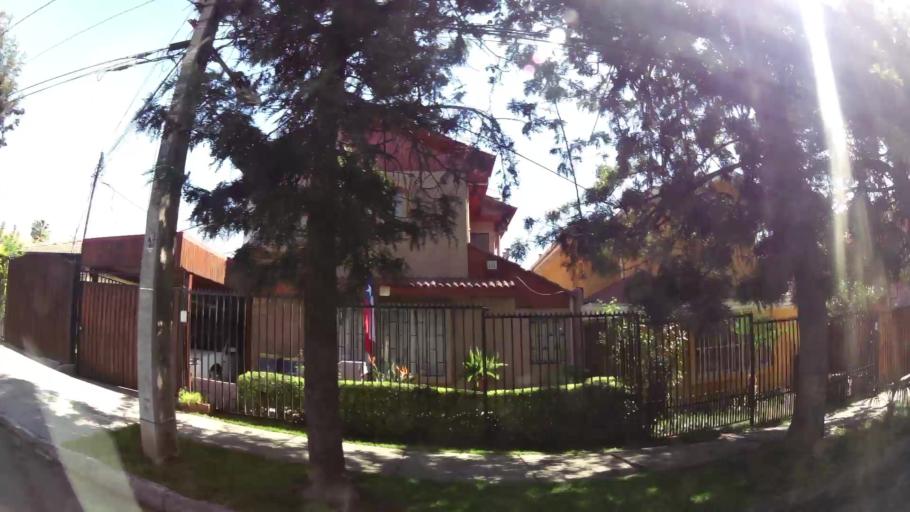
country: CL
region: Santiago Metropolitan
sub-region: Provincia de Santiago
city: Villa Presidente Frei, Nunoa, Santiago, Chile
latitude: -33.5276
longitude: -70.5668
